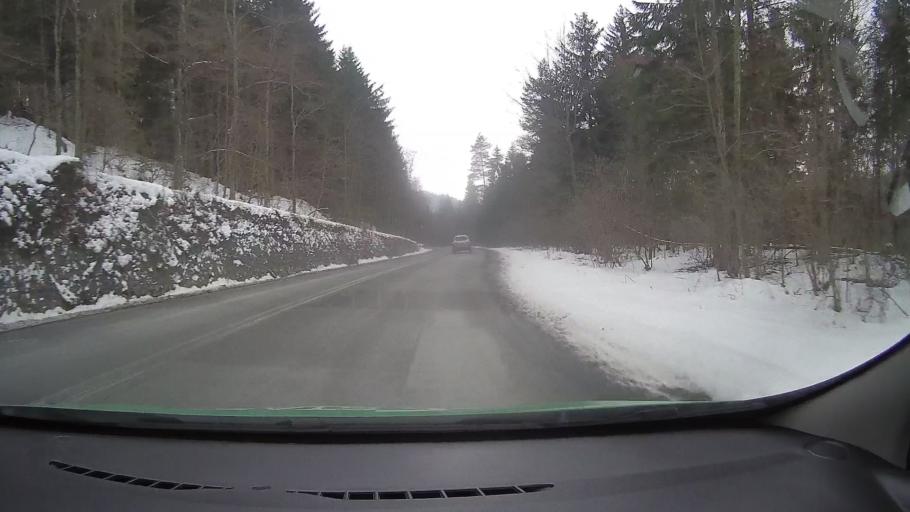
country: RO
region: Brasov
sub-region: Oras Predeal
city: Predeal
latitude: 45.5212
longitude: 25.5080
